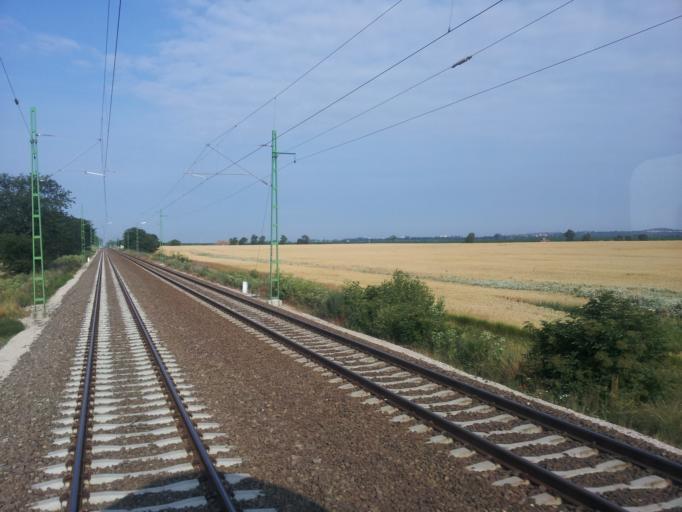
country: HU
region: Fejer
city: Pakozd
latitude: 47.1749
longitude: 18.5262
